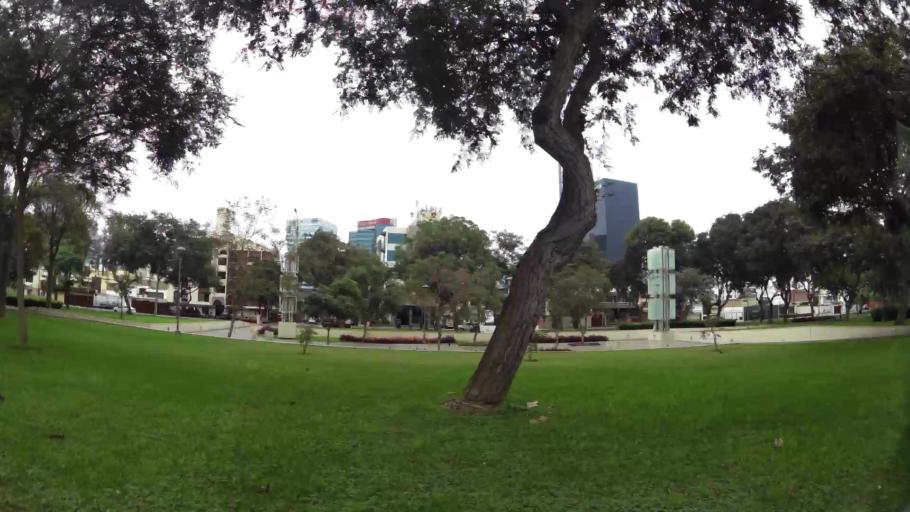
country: PE
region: Lima
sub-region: Lima
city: San Luis
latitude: -12.0941
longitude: -77.0186
